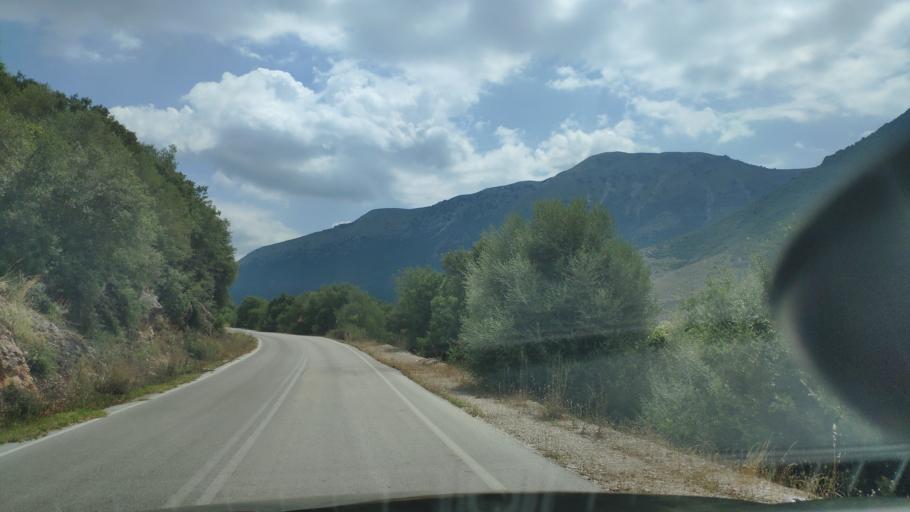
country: GR
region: Epirus
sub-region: Nomos Artas
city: Kampi
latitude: 39.2677
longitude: 20.9255
